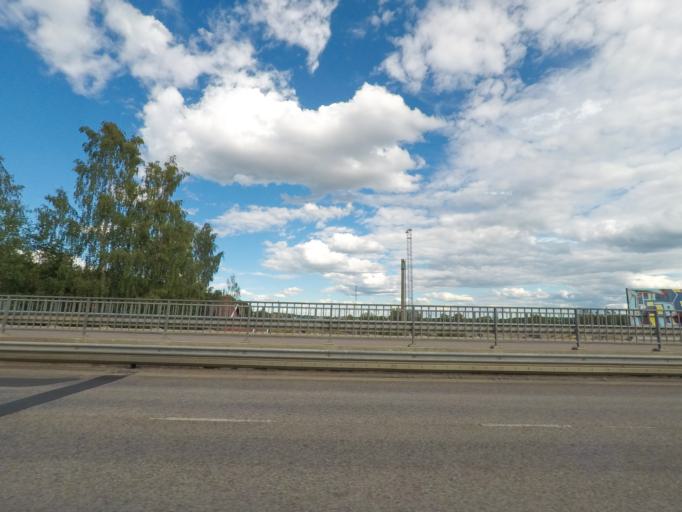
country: FI
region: Paijanne Tavastia
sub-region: Lahti
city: Lahti
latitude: 60.9774
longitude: 25.6393
